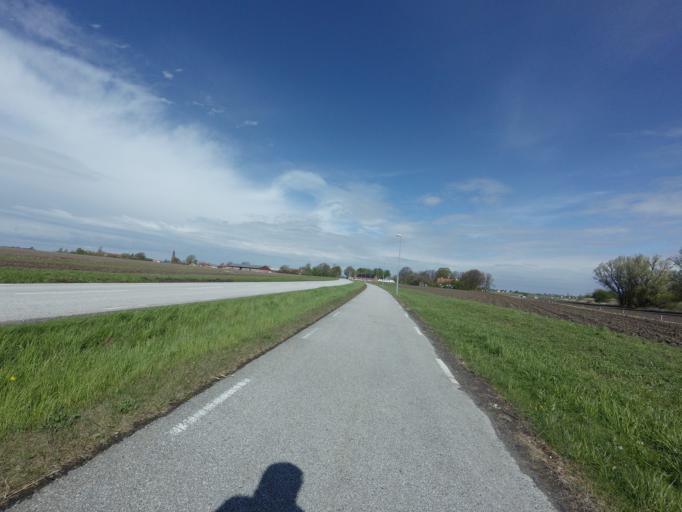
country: SE
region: Skane
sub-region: Malmo
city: Tygelsjo
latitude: 55.4984
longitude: 12.9996
